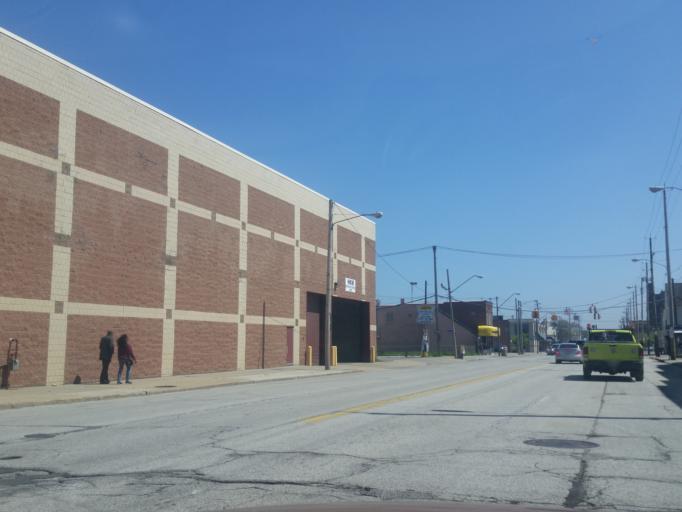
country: US
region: Ohio
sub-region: Cuyahoga County
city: Cleveland
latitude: 41.5083
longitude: -81.6674
